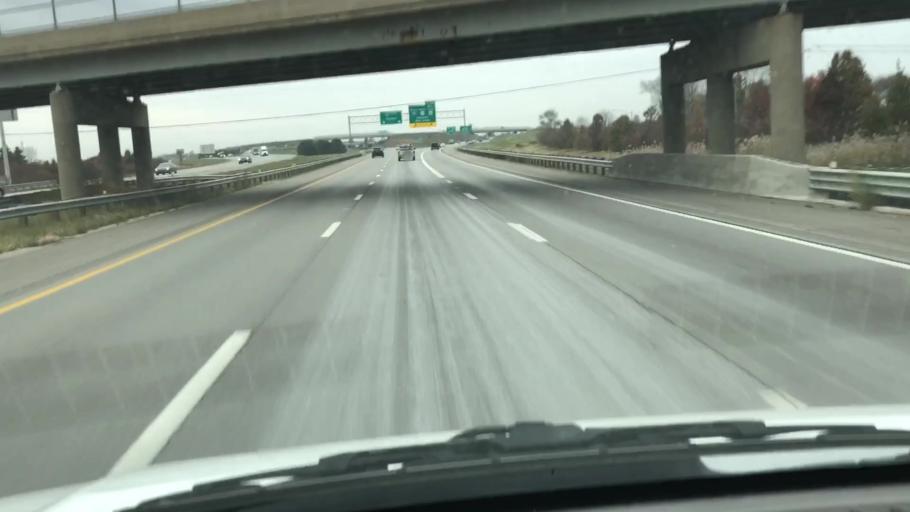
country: US
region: Ohio
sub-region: Wood County
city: Perrysburg
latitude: 41.5386
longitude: -83.6153
